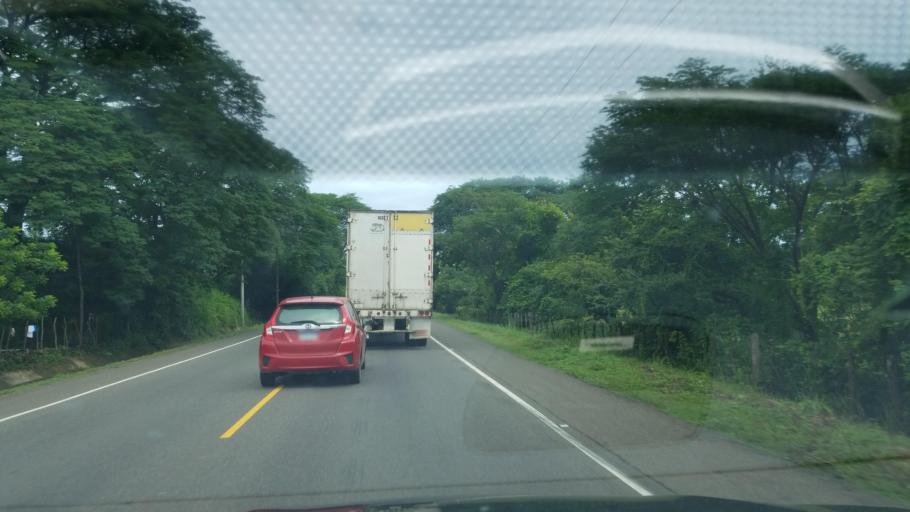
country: HN
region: Valle
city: Goascoran
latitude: 13.5404
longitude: -87.6165
